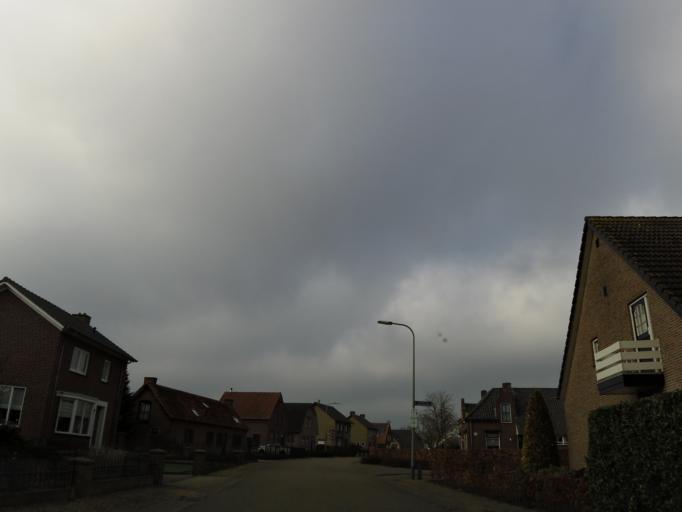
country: NL
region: North Brabant
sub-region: Gemeente Cuijk
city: Cuijk
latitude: 51.7256
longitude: 5.9125
